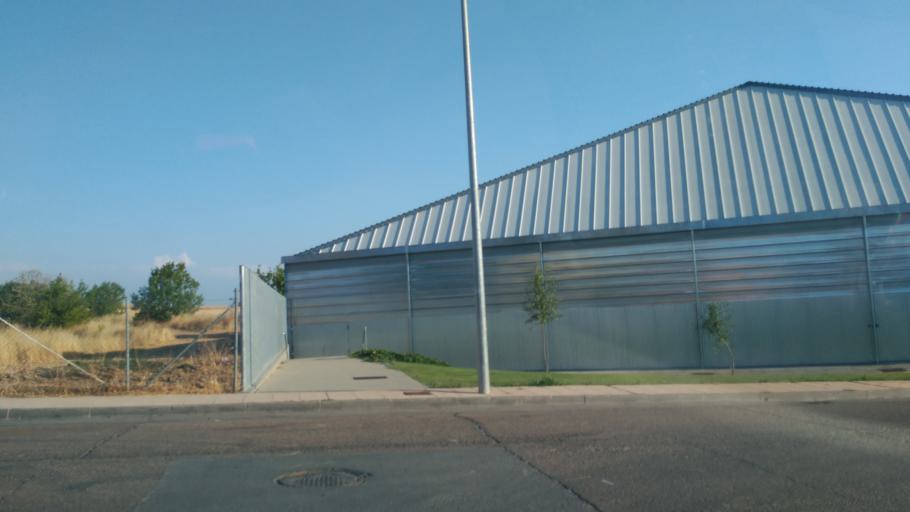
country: ES
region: Castille and Leon
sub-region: Provincia de Salamanca
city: Carbajosa de la Sagrada
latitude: 40.9326
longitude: -5.6458
